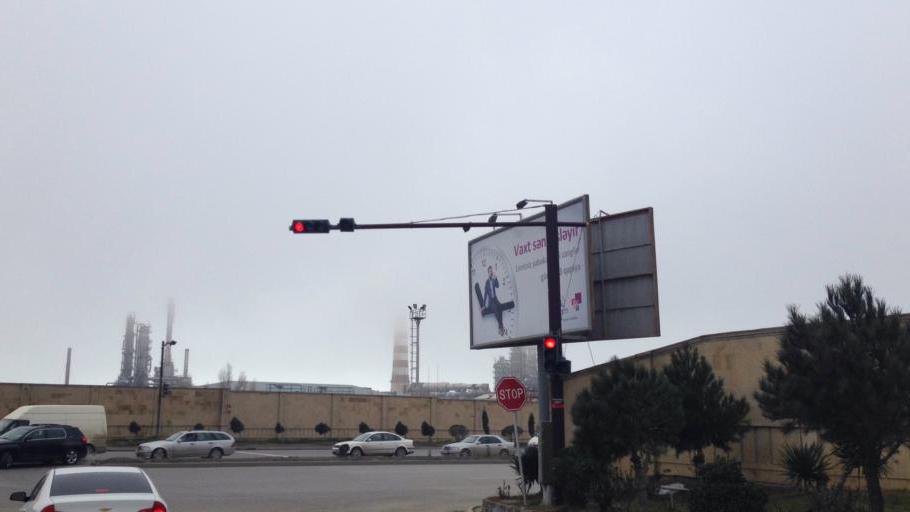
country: AZ
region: Baki
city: Baku
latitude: 40.3768
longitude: 49.9139
